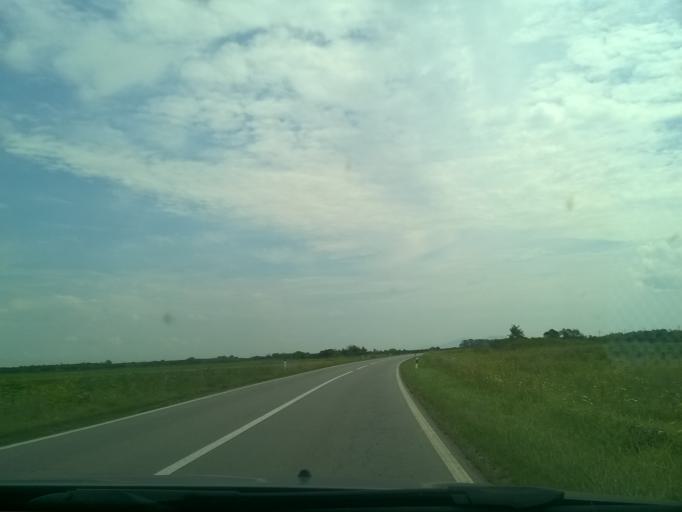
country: RS
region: Autonomna Pokrajina Vojvodina
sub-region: Juznobanatski Okrug
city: Plandiste
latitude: 45.2561
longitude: 21.0934
